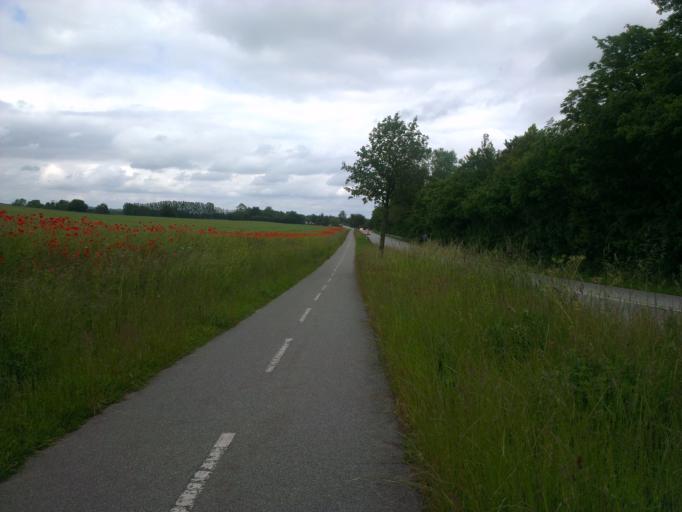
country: DK
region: Capital Region
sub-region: Frederikssund Kommune
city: Skibby
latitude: 55.6780
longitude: 11.9410
